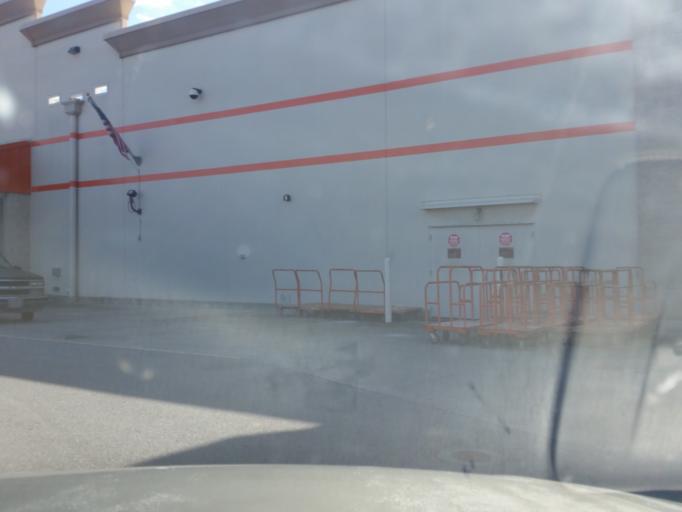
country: US
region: Florida
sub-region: Escambia County
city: Brent
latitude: 30.4756
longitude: -87.2276
